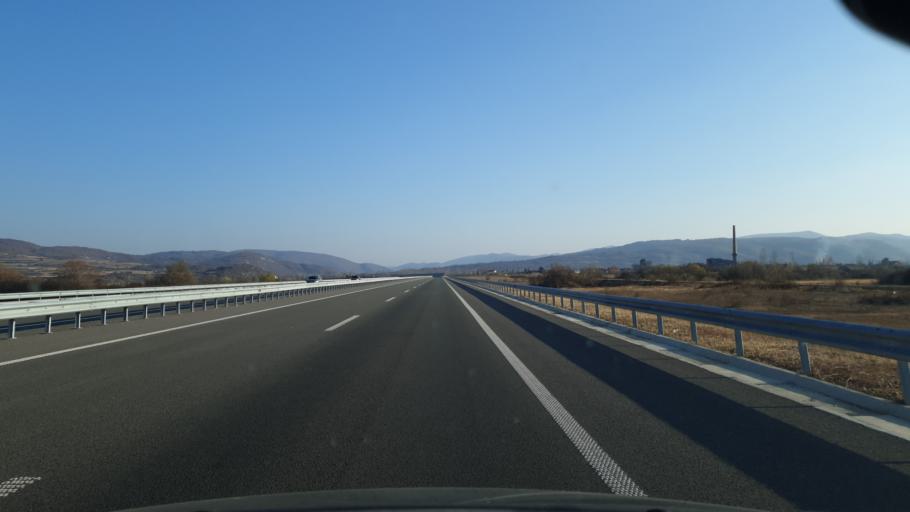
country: RS
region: Central Serbia
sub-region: Pirotski Okrug
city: Pirot
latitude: 43.0812
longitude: 22.6632
